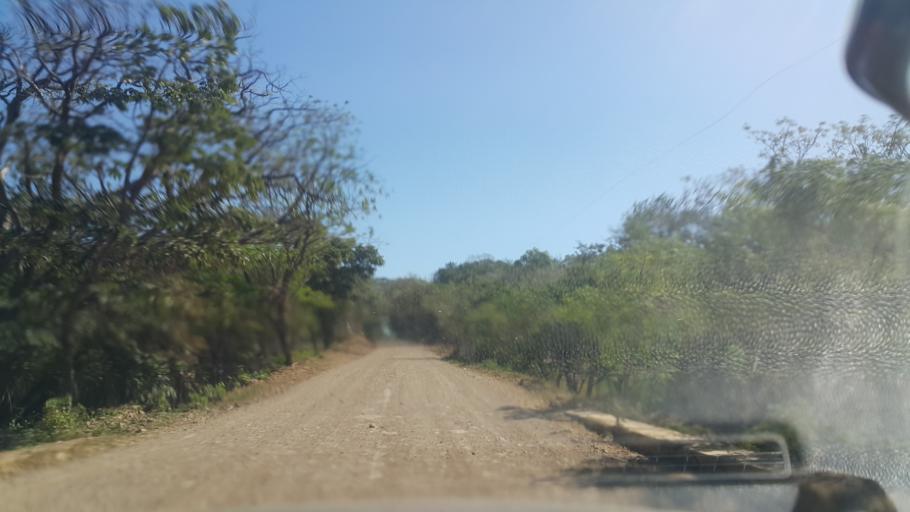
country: NI
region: Rivas
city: San Juan del Sur
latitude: 11.2822
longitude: -85.8892
